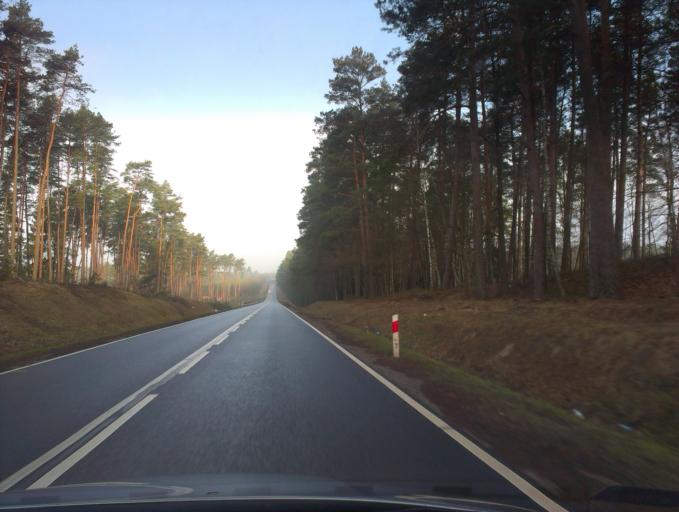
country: PL
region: West Pomeranian Voivodeship
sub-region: Powiat koszalinski
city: Bobolice
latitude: 54.0598
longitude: 16.4142
